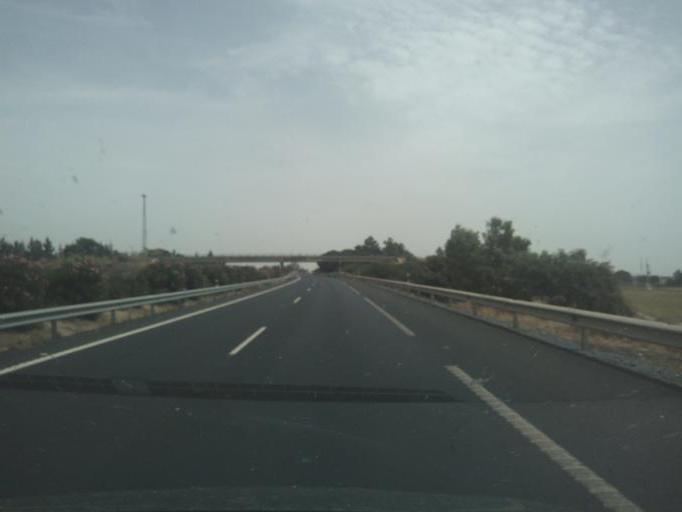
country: ES
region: Andalusia
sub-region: Provincia de Huelva
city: Villarrasa
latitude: 37.3442
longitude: -6.6294
